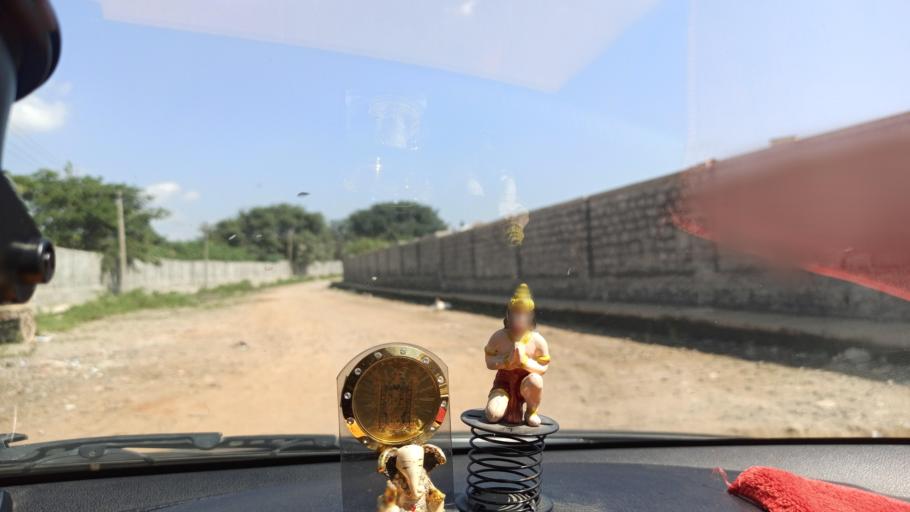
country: IN
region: Karnataka
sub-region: Bangalore Urban
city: Bangalore
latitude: 12.9606
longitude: 77.6964
